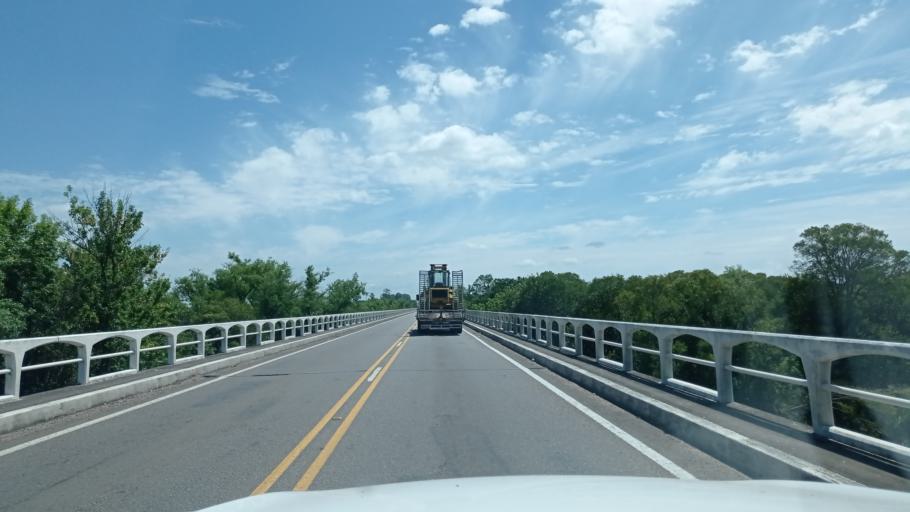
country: UY
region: Florida
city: Cardal
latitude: -34.3657
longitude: -56.2495
